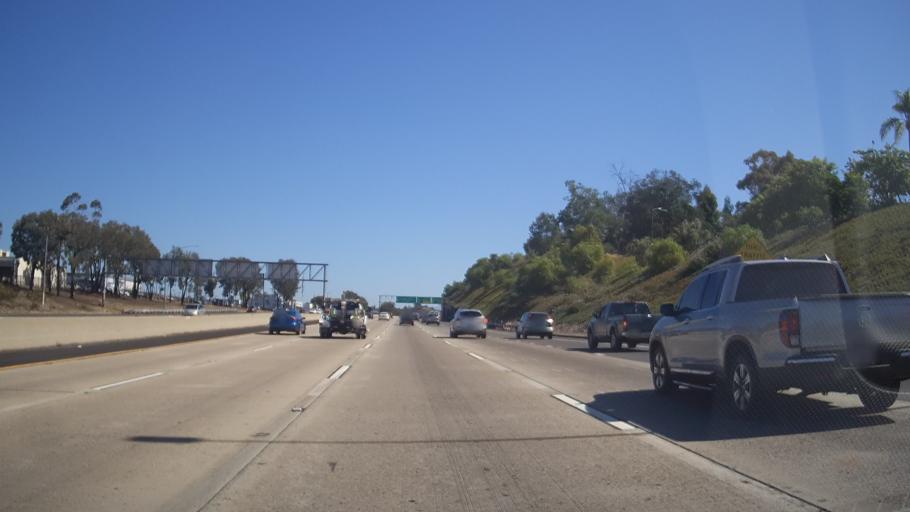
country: US
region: California
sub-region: San Diego County
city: La Mesa
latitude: 32.7717
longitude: -117.0186
